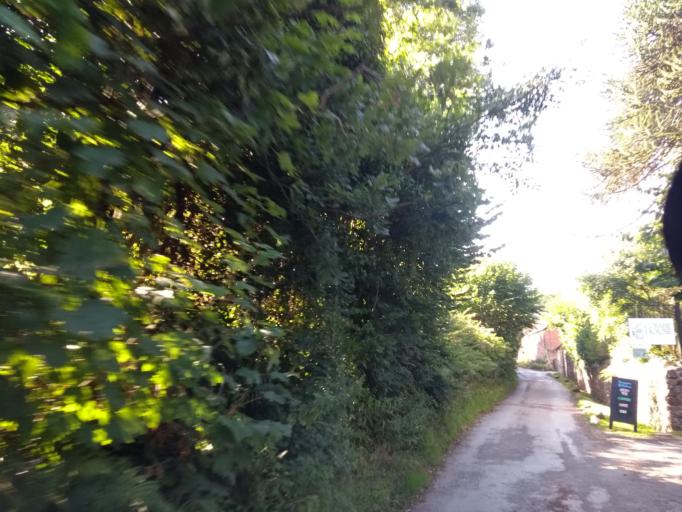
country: GB
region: England
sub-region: Somerset
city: Bishops Lydeard
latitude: 51.1579
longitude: -3.2146
